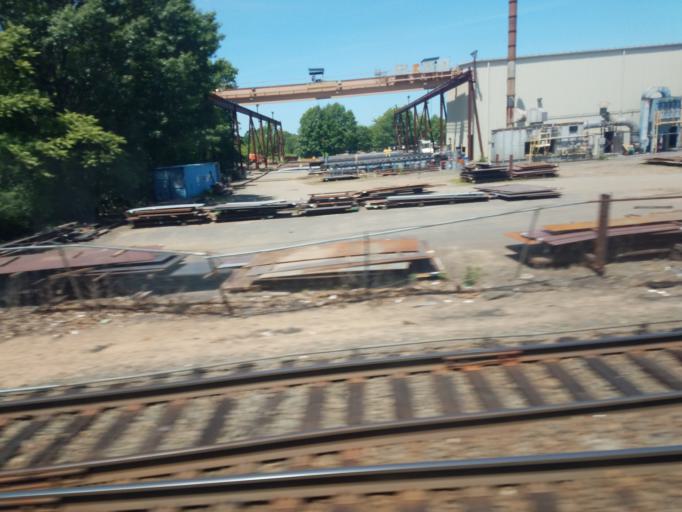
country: US
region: Connecticut
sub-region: New Haven County
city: Wallingford
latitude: 41.4764
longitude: -72.8144
